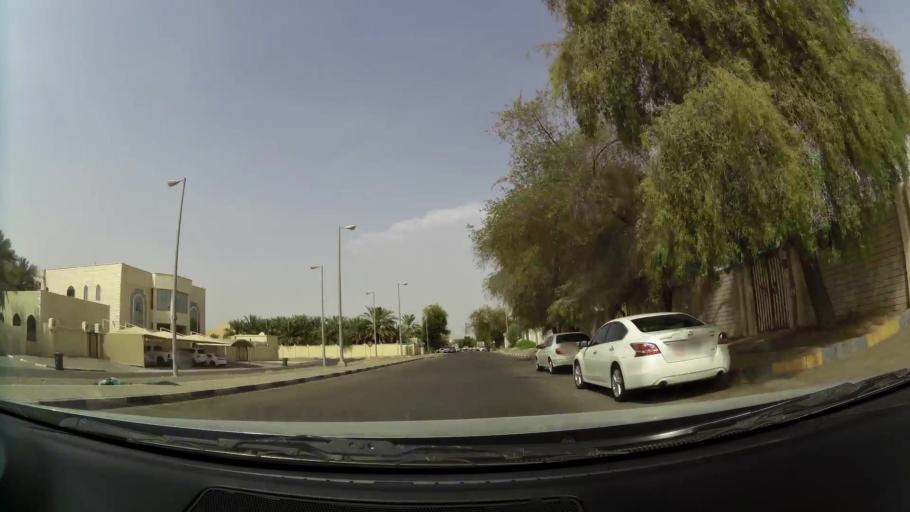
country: AE
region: Abu Dhabi
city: Al Ain
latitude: 24.1854
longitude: 55.6301
